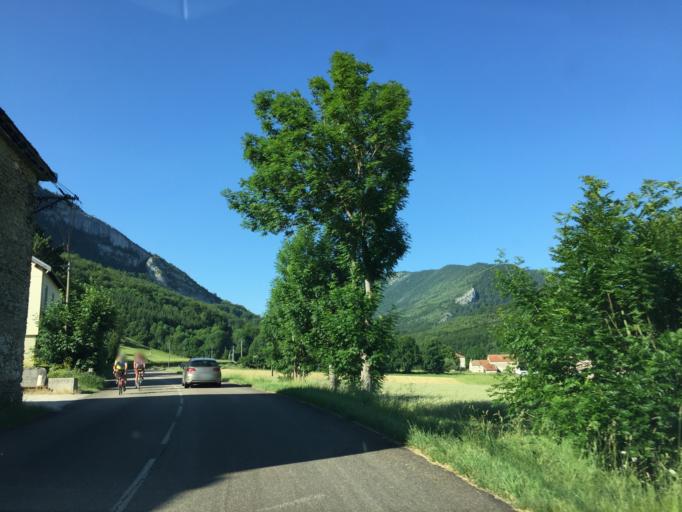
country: FR
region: Rhone-Alpes
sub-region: Departement de la Drome
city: Saint-Laurent-en-Royans
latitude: 44.9578
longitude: 5.4066
